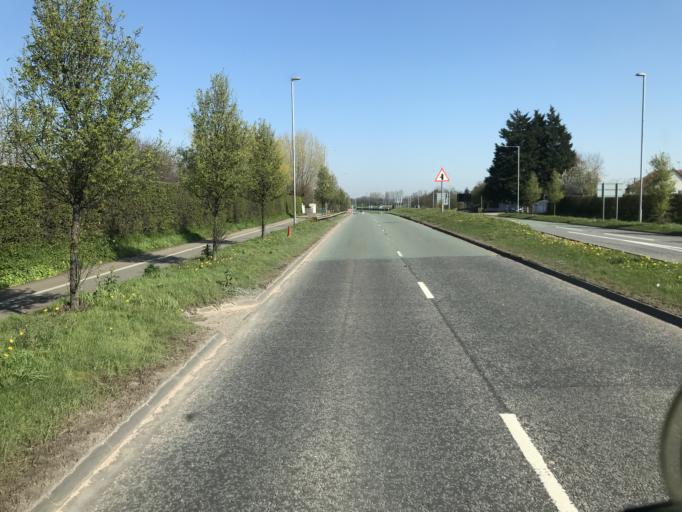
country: GB
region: England
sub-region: Cheshire West and Chester
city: Hoole
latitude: 53.1887
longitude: -2.8529
